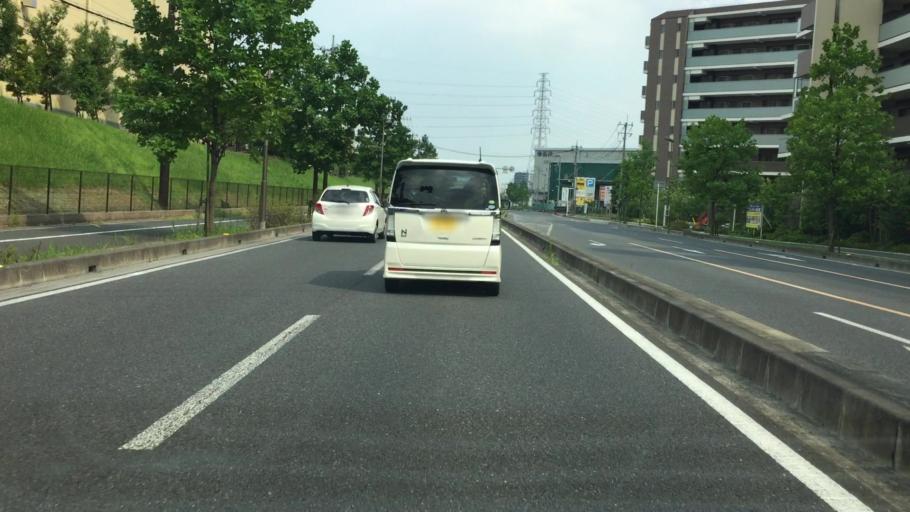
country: JP
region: Chiba
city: Nagareyama
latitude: 35.8544
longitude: 139.8712
